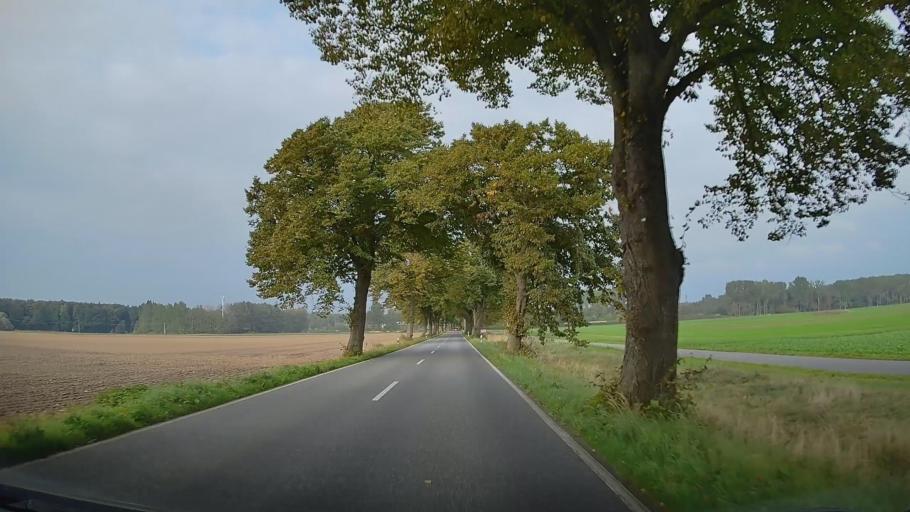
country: DE
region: Mecklenburg-Vorpommern
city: Bad Doberan
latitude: 54.1337
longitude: 11.8350
